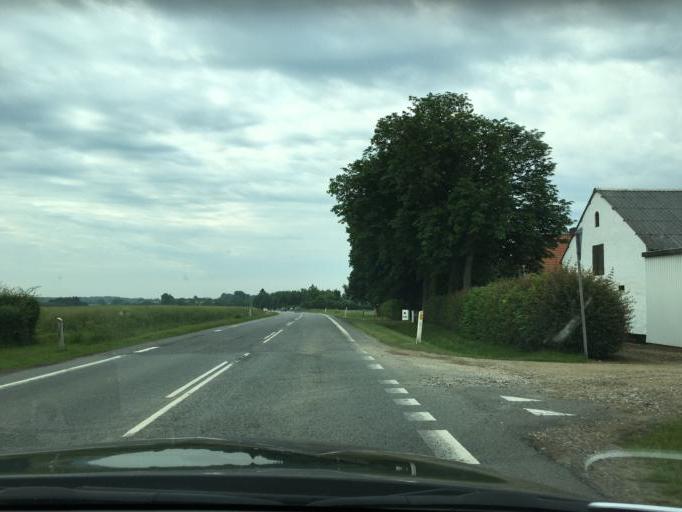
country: DK
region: South Denmark
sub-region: Kolding Kommune
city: Kolding
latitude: 55.5931
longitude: 9.4933
